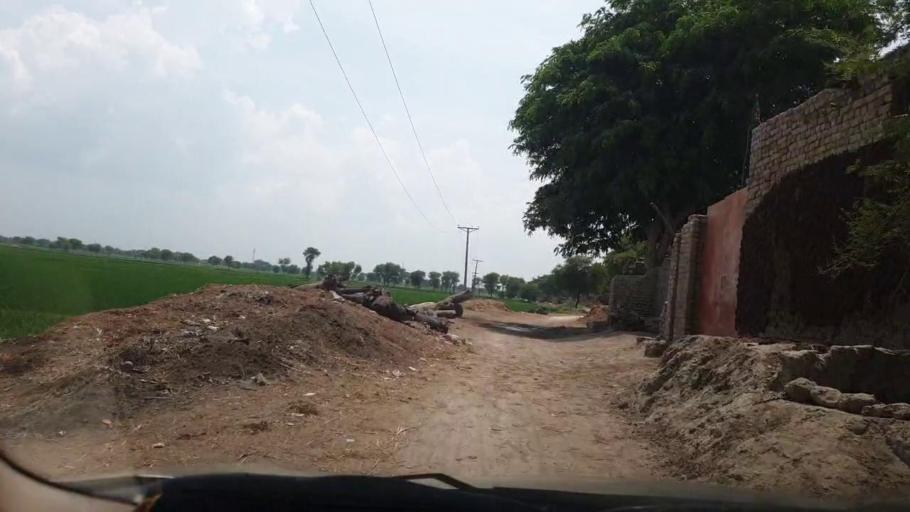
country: PK
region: Sindh
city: Larkana
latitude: 27.5937
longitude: 68.1223
